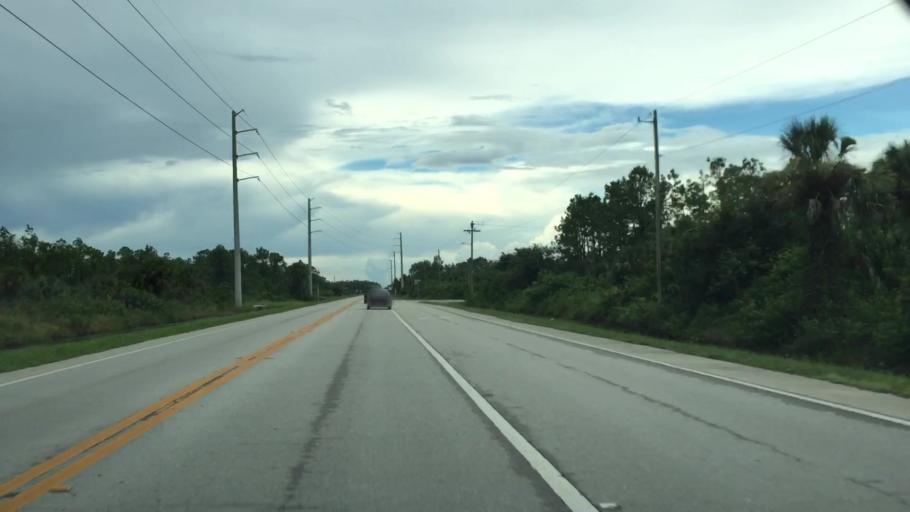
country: US
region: Florida
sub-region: Collier County
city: Orangetree
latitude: 26.3162
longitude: -81.5950
